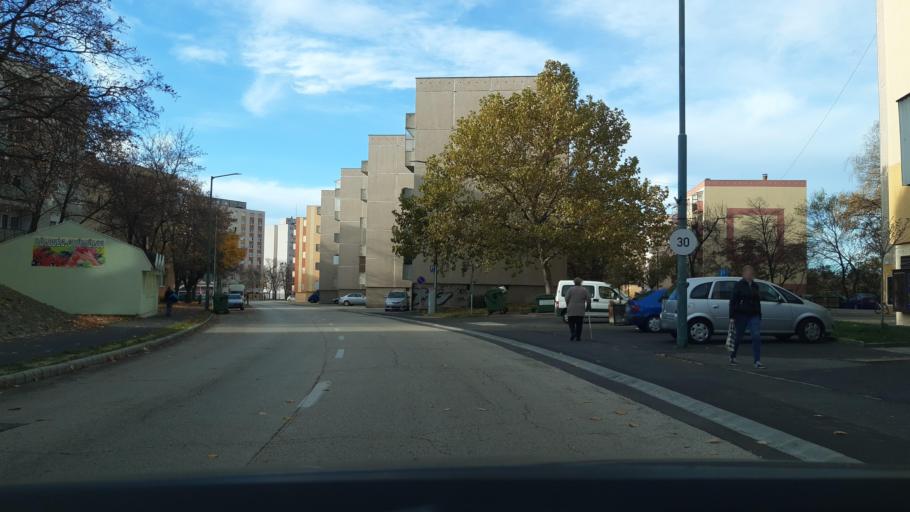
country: HU
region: Veszprem
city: Ajka
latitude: 47.1076
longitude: 17.5606
